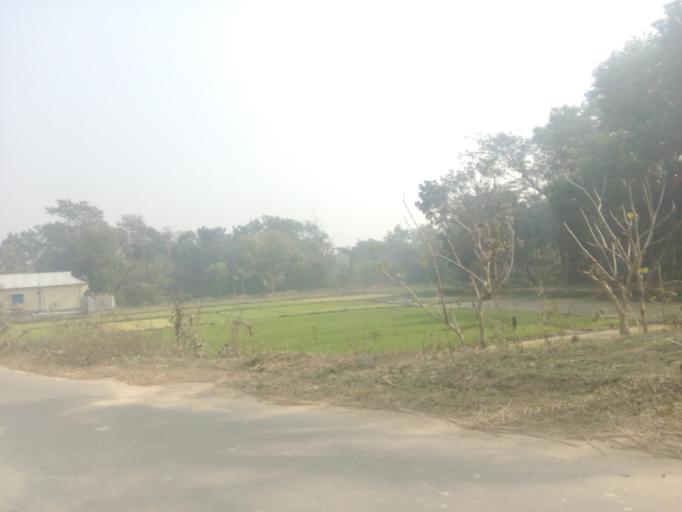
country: IN
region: Tripura
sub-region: West Tripura
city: Sonamura
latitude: 23.3218
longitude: 91.2782
